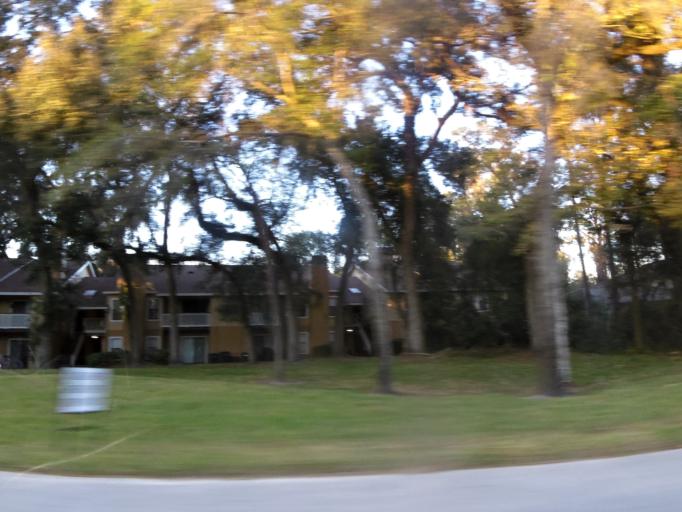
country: US
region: Florida
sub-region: Saint Johns County
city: Fruit Cove
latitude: 30.2059
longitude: -81.6089
